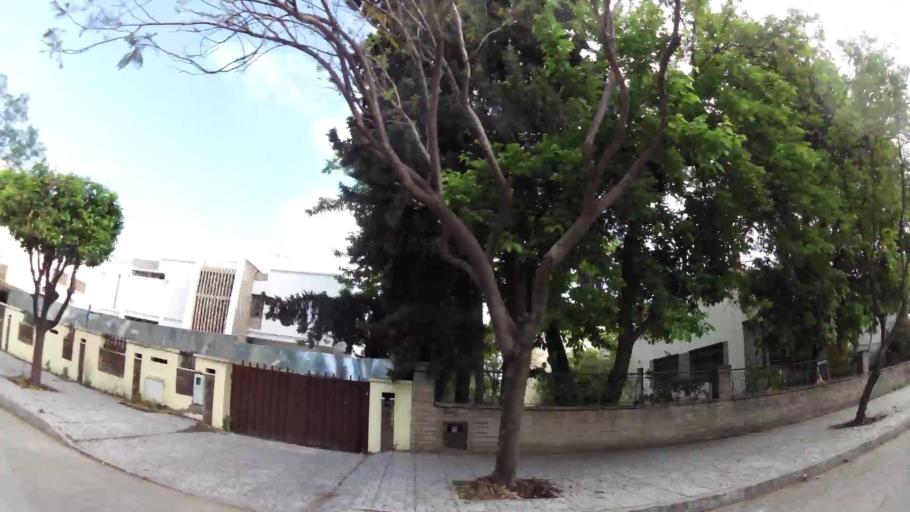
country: MA
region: Fes-Boulemane
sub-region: Fes
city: Fes
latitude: 34.0314
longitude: -5.0113
